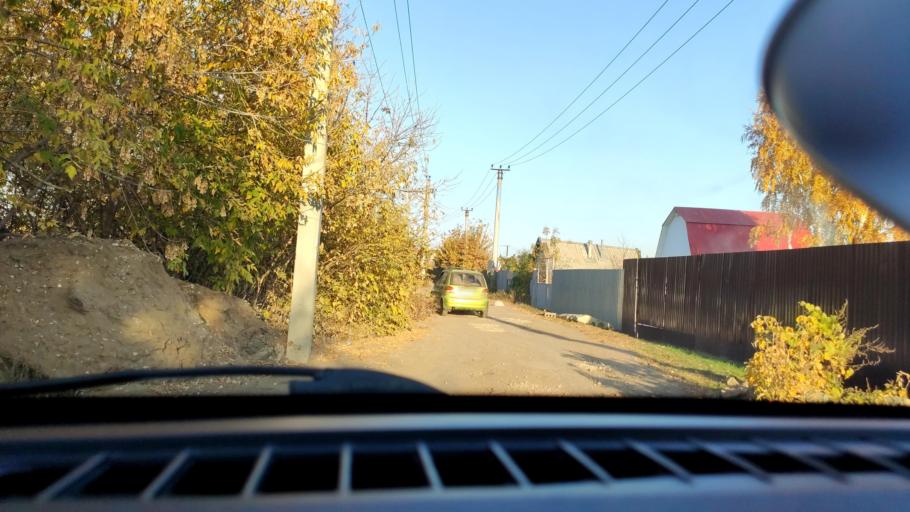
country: RU
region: Samara
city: Samara
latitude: 53.1826
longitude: 50.2252
